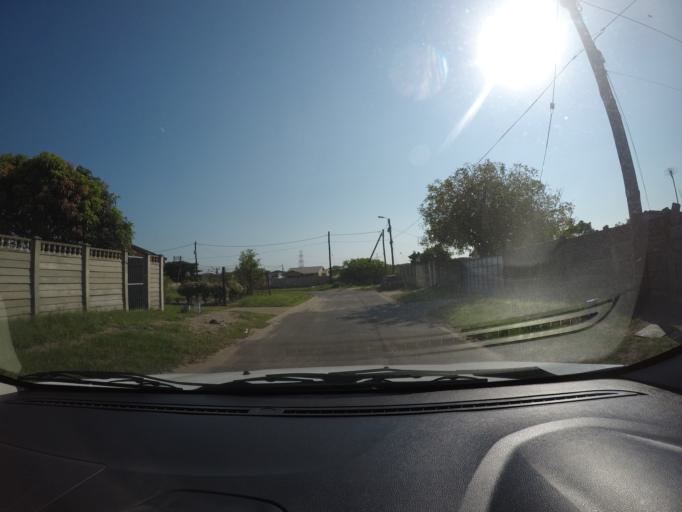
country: ZA
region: KwaZulu-Natal
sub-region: uThungulu District Municipality
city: Richards Bay
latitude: -28.7208
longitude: 32.0359
